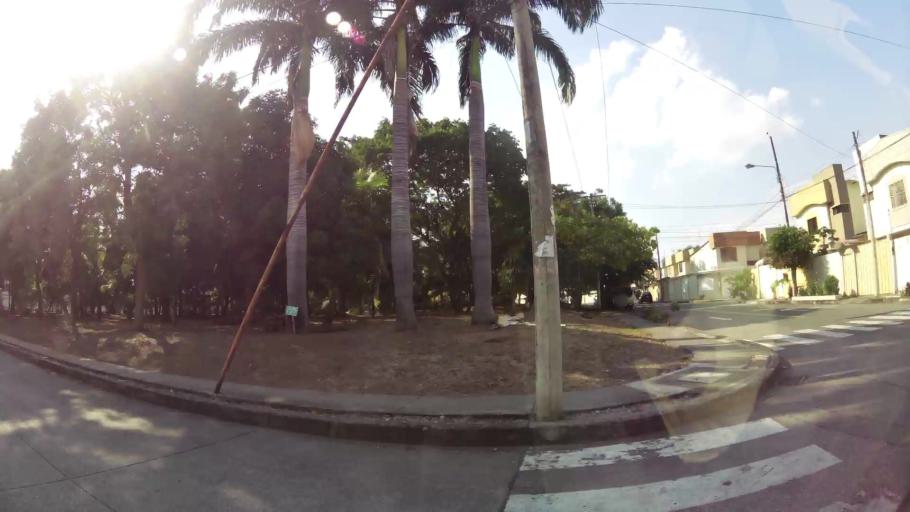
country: EC
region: Guayas
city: Guayaquil
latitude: -2.1379
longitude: -79.9259
